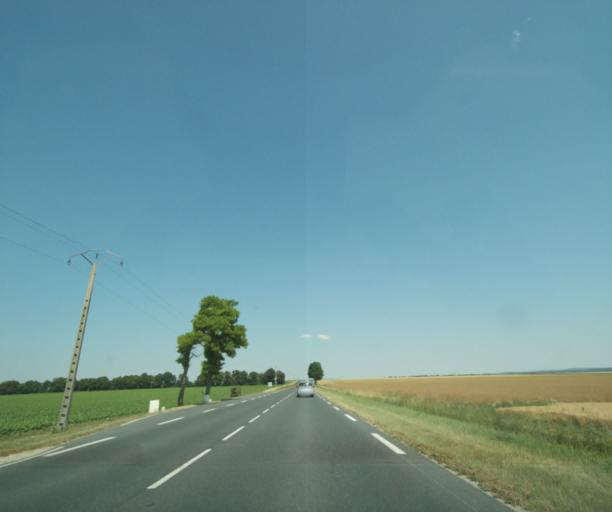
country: FR
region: Champagne-Ardenne
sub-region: Departement de la Marne
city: Mourmelon-le-Grand
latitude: 49.0852
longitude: 4.2786
